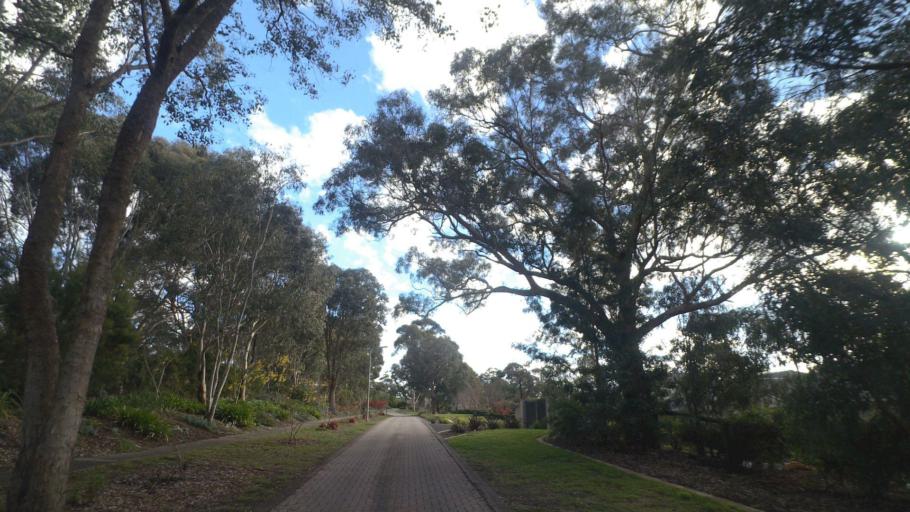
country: AU
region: Victoria
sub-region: Banyule
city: Lower Plenty
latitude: -37.7396
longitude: 145.1187
